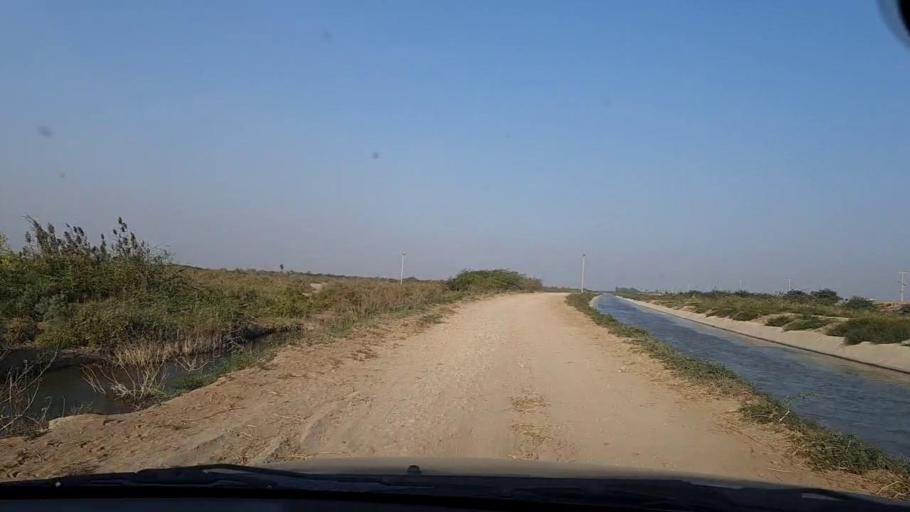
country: PK
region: Sindh
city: Chuhar Jamali
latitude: 24.2802
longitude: 67.7420
